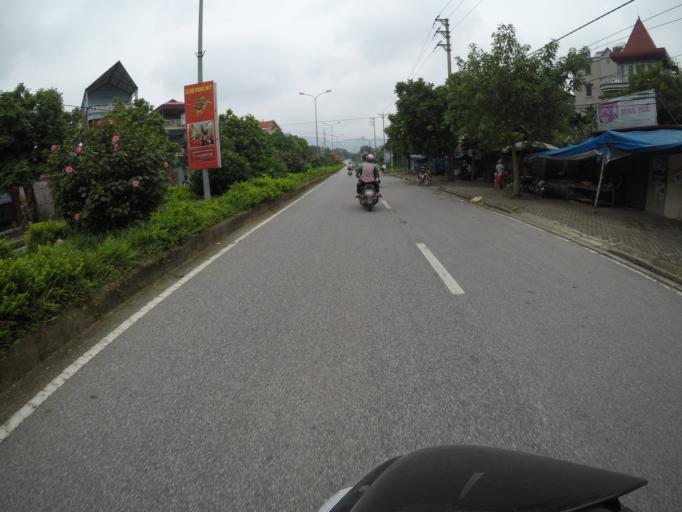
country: VN
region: Ha Noi
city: Soc Son
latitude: 21.2749
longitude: 105.8498
